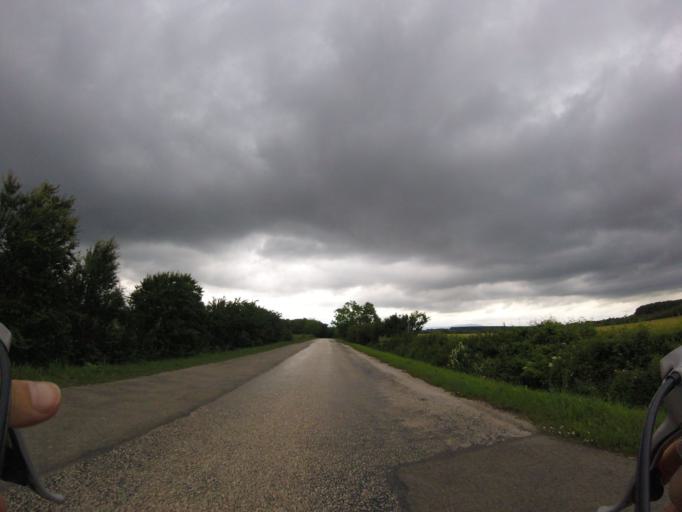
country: HU
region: Baranya
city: Pellerd
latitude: 45.9680
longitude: 18.1526
